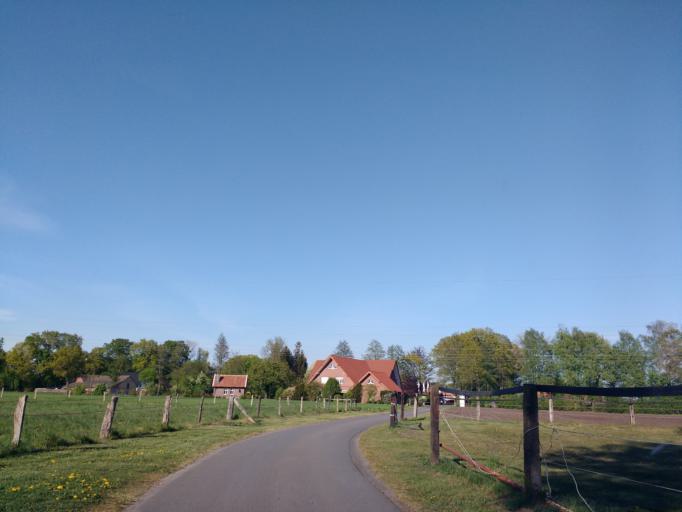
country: DE
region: North Rhine-Westphalia
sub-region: Regierungsbezirk Detmold
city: Delbruck
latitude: 51.7572
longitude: 8.5745
